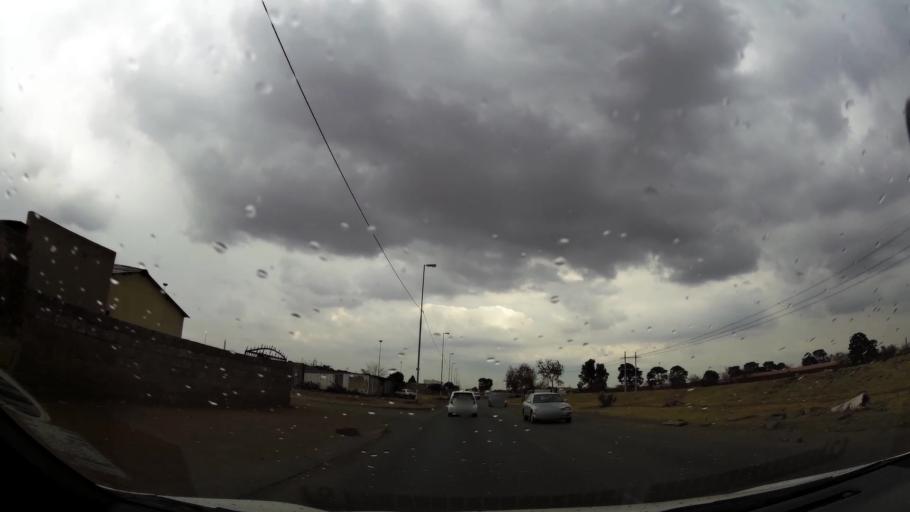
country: ZA
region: Gauteng
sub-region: Ekurhuleni Metropolitan Municipality
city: Germiston
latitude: -26.3458
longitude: 28.1440
